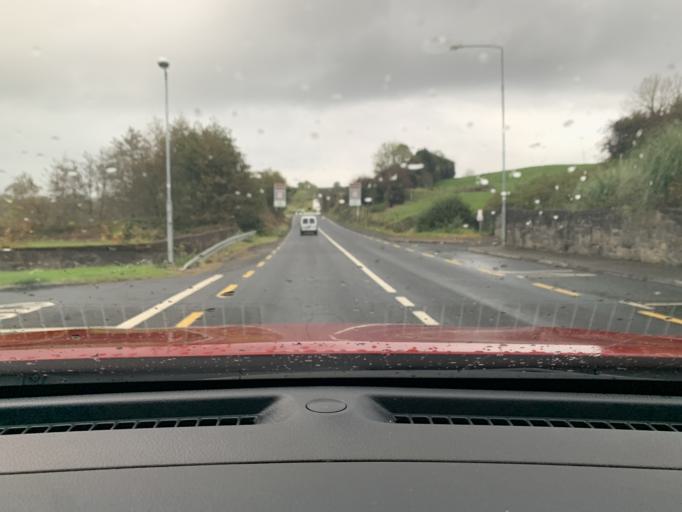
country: IE
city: Ballisodare
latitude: 54.2160
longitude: -8.5105
